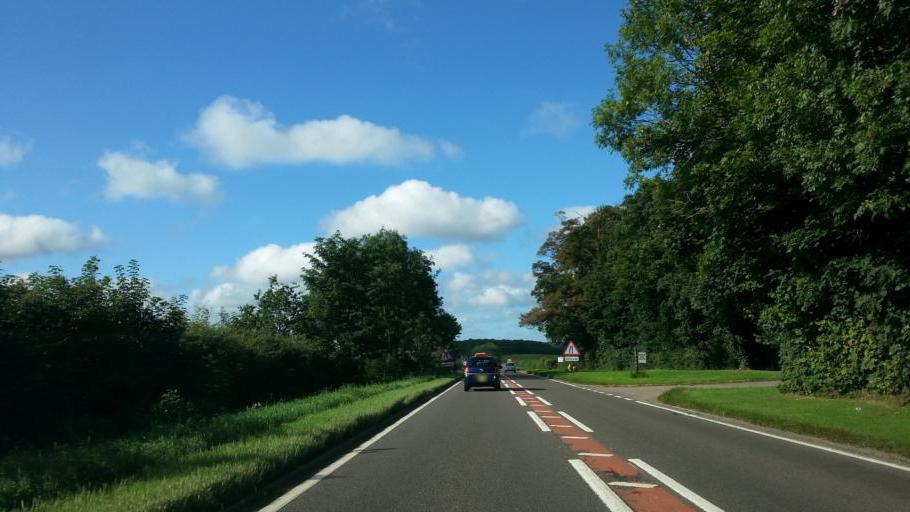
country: GB
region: England
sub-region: Northamptonshire
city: Northampton
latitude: 52.3009
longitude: -0.8260
